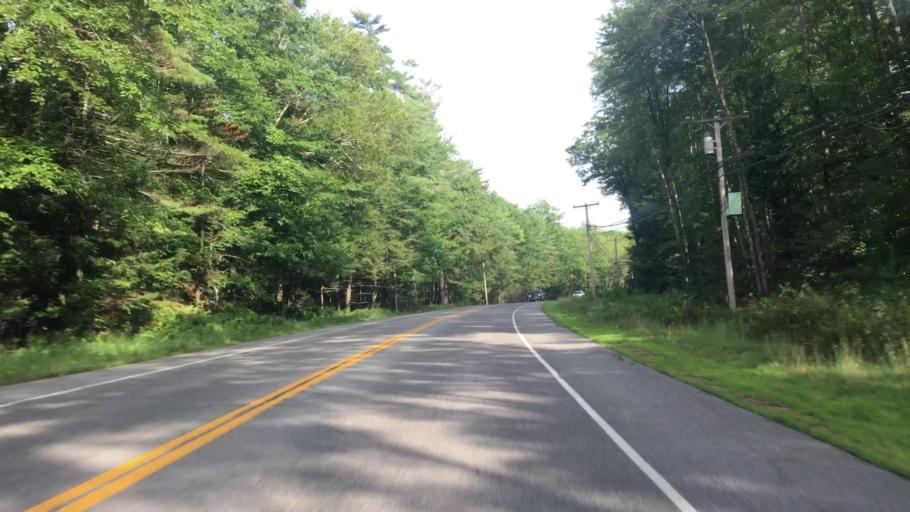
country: US
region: Maine
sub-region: York County
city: Limington
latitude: 43.7392
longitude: -70.6725
